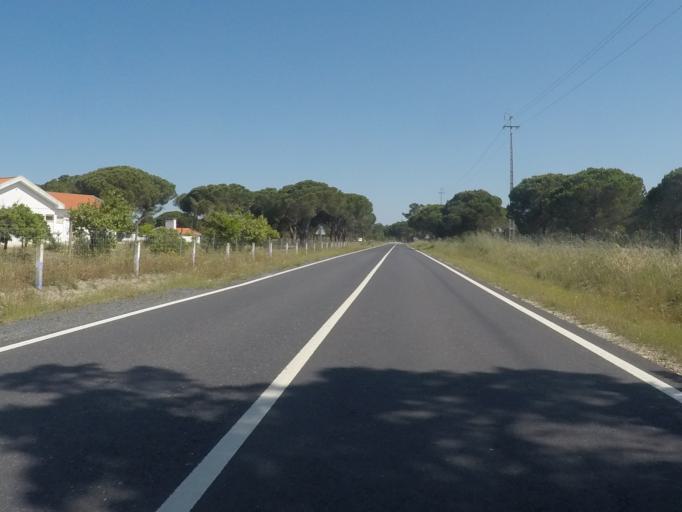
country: PT
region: Setubal
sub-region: Grandola
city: Grandola
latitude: 38.2701
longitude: -8.7273
